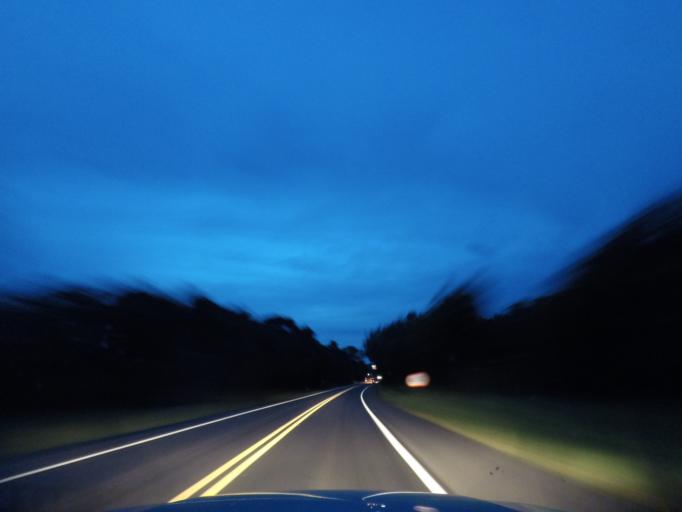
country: BR
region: Bahia
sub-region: Iraquara
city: Iraquara
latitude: -12.4807
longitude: -41.3566
